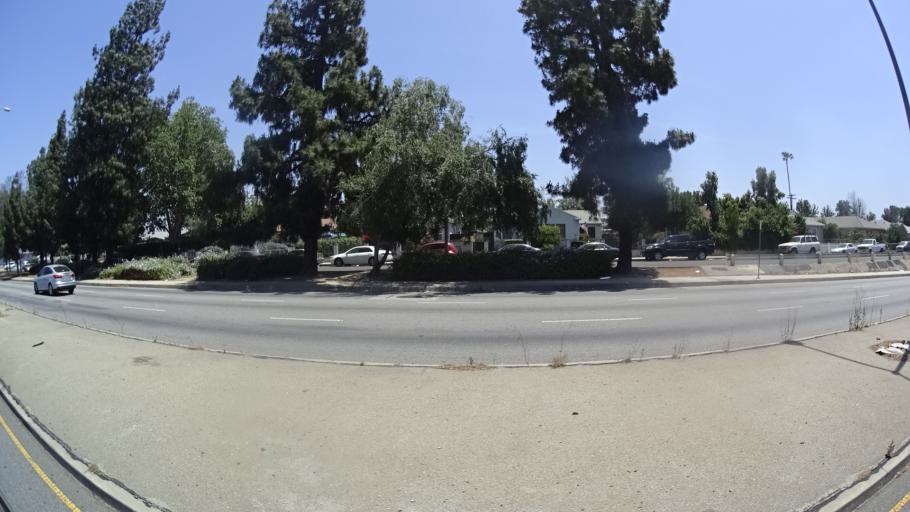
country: US
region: California
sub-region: Los Angeles County
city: Van Nuys
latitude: 34.2170
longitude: -118.4663
